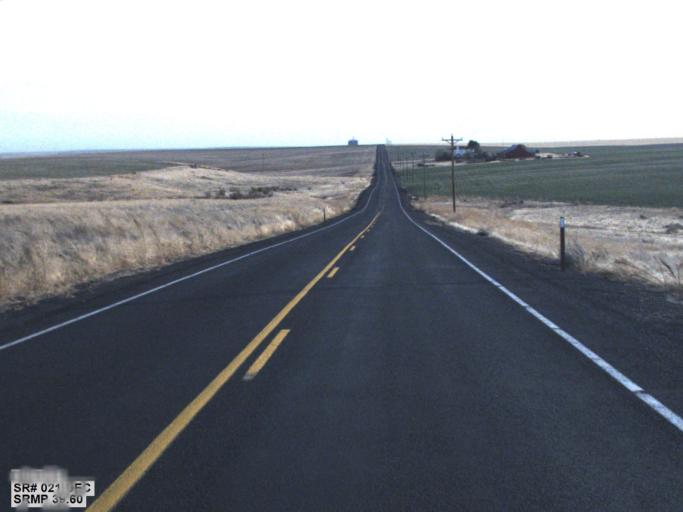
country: US
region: Washington
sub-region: Adams County
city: Ritzville
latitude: 47.1228
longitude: -118.6652
